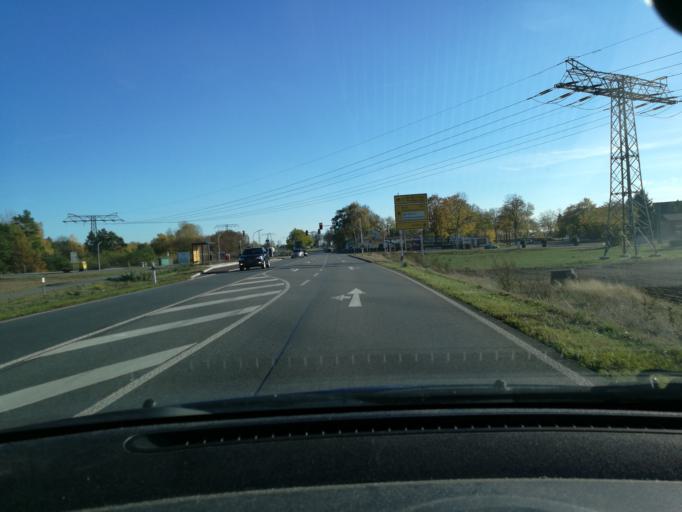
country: DE
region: Brandenburg
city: Perleberg
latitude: 53.1027
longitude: 11.8300
